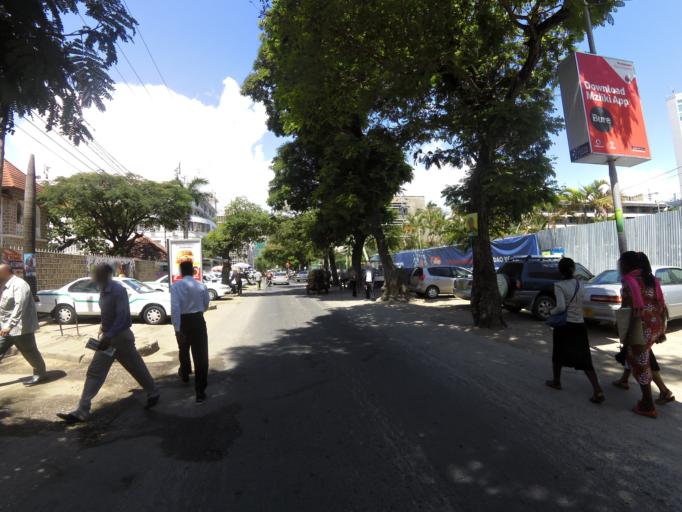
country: TZ
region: Dar es Salaam
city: Dar es Salaam
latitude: -6.8150
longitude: 39.2914
